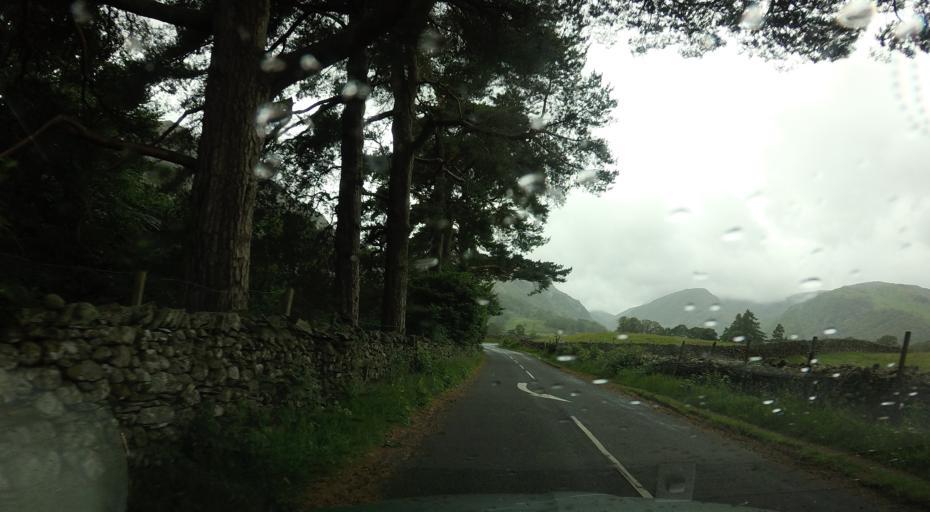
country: GB
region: England
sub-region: Cumbria
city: Keswick
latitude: 54.5167
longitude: -3.1496
